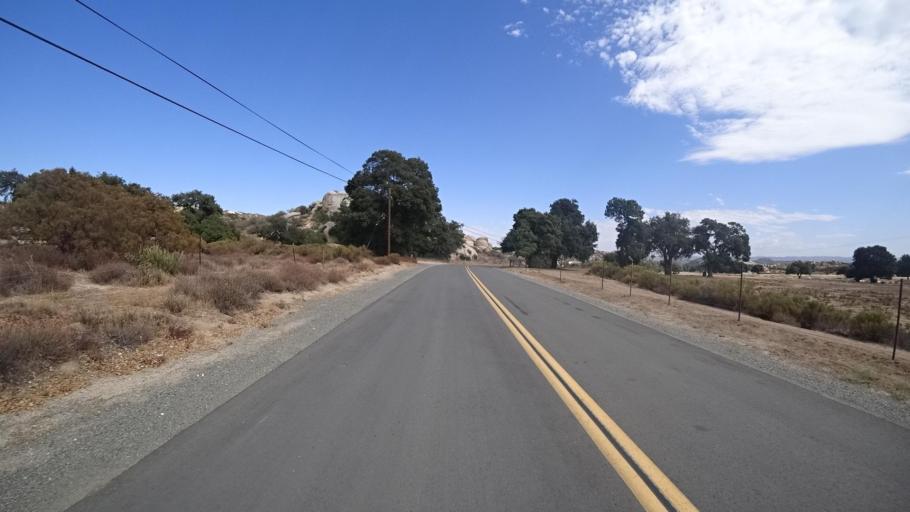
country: MX
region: Baja California
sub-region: Tecate
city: Cereso del Hongo
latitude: 32.6448
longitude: -116.2812
